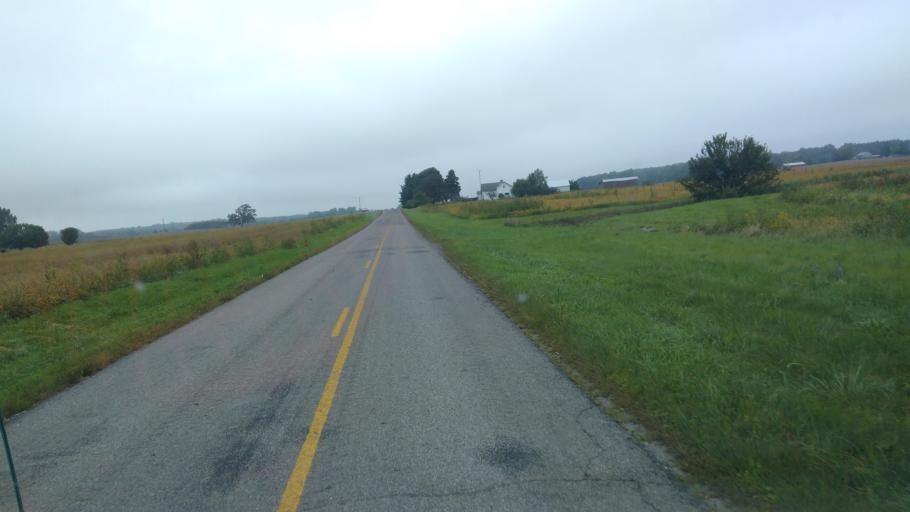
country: US
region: Ohio
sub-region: Hardin County
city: Kenton
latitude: 40.5461
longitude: -83.6344
